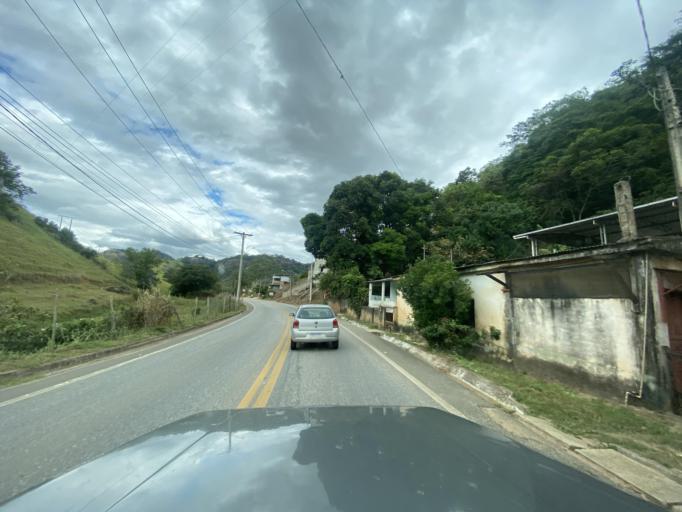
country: BR
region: Espirito Santo
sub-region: Jeronimo Monteiro
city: Jeronimo Monteiro
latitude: -20.7652
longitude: -41.4470
